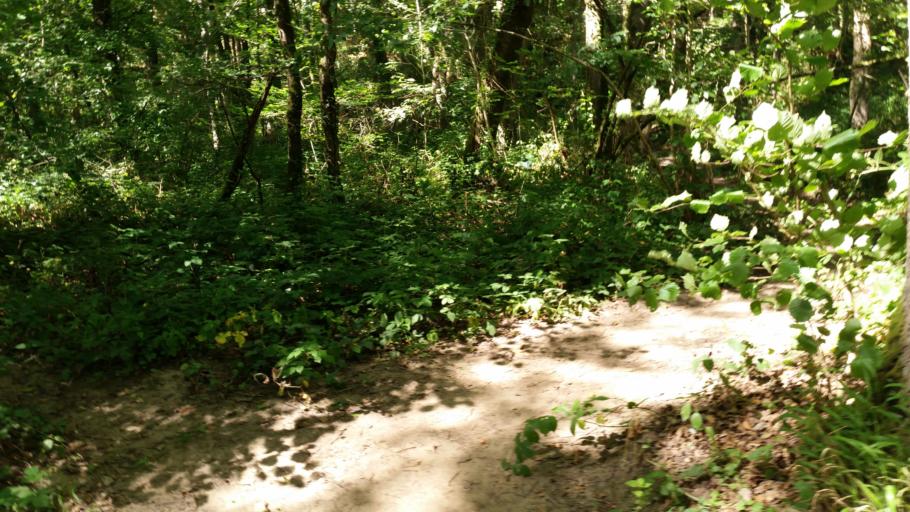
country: FR
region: Lower Normandy
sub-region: Departement de l'Orne
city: Briouze
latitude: 48.8281
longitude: -0.3844
